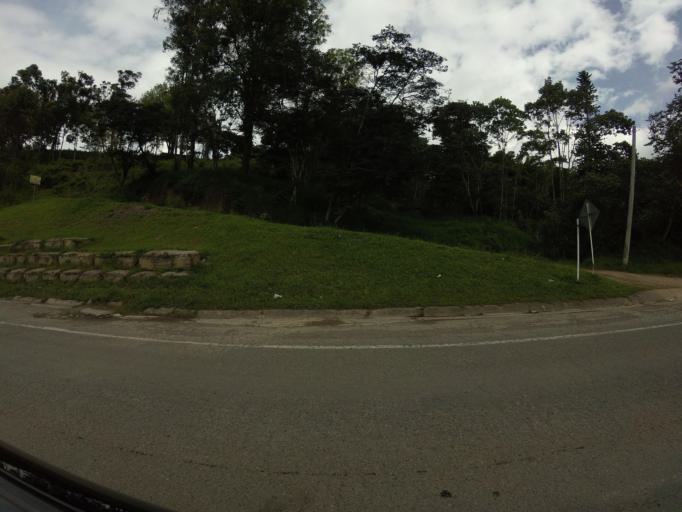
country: CO
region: Cundinamarca
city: Silvania
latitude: 4.4351
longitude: -74.3856
